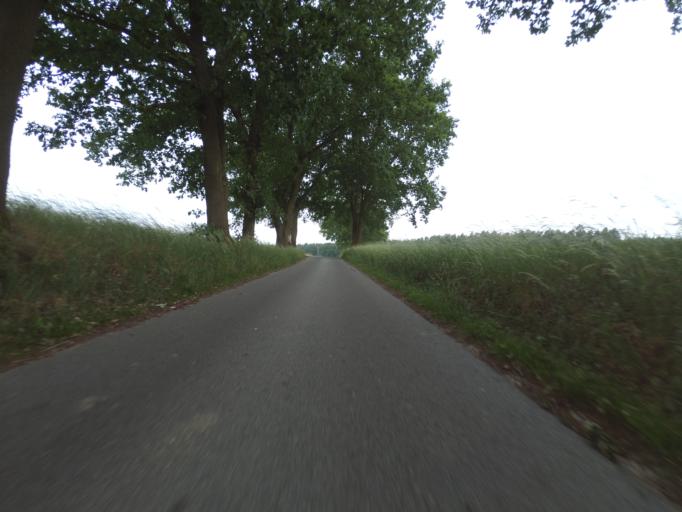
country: DE
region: Mecklenburg-Vorpommern
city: Lubz
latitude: 53.5120
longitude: 12.0807
